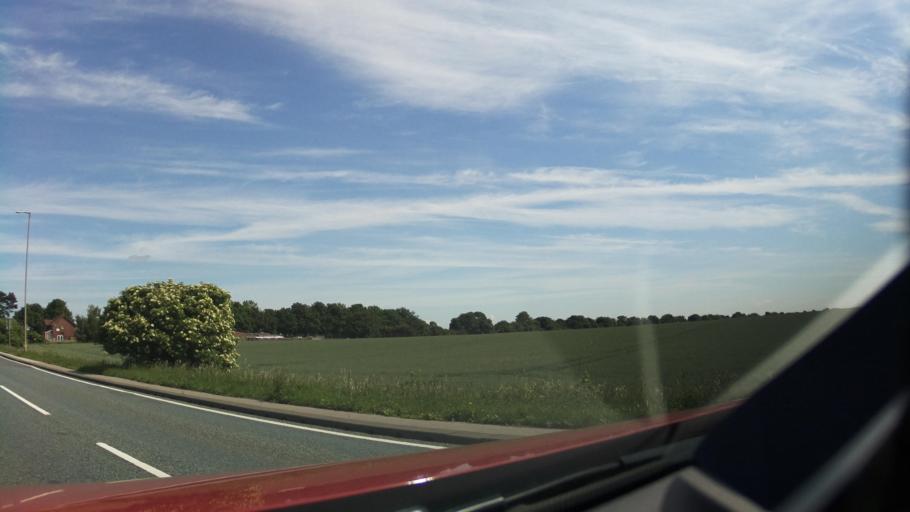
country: GB
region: England
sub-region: Lincolnshire
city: Burton
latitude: 53.2889
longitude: -0.5407
